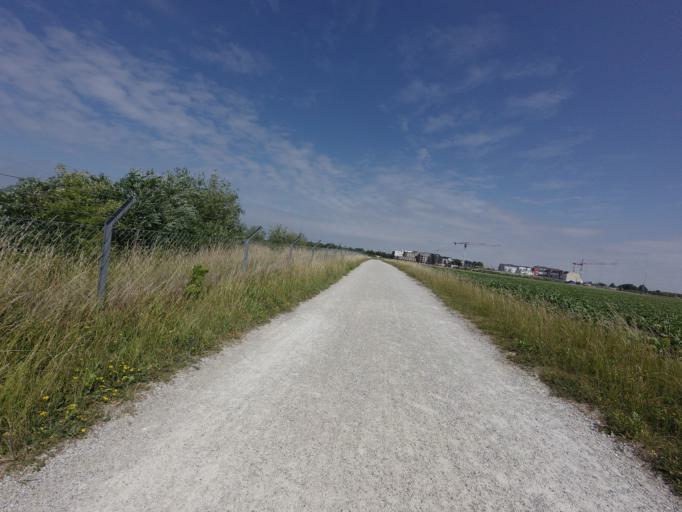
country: SE
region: Skane
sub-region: Malmo
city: Bunkeflostrand
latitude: 55.5651
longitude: 12.9431
